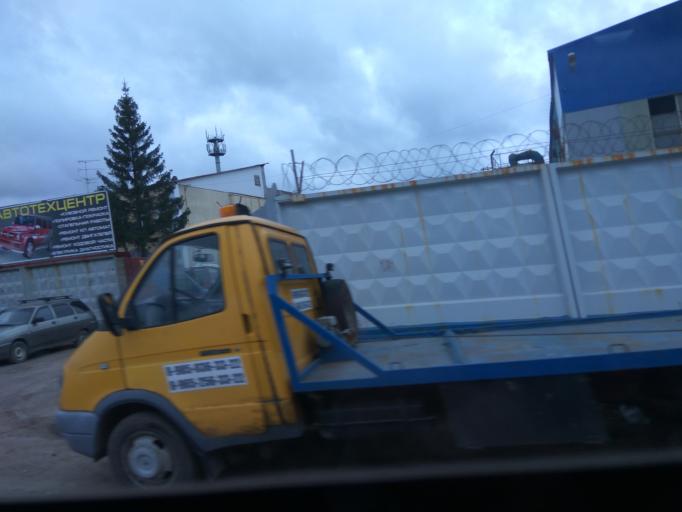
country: RU
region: Moskovskaya
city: Malyshevo
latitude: 55.5157
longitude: 38.3417
